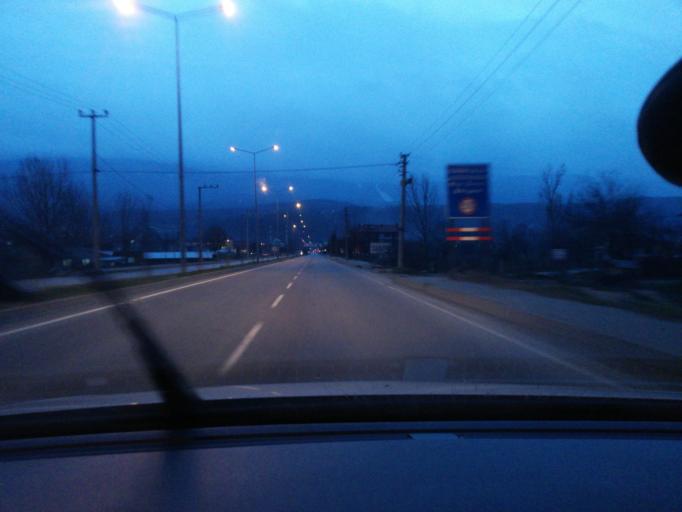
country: TR
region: Bolu
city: Bolu
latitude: 40.6961
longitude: 31.6190
